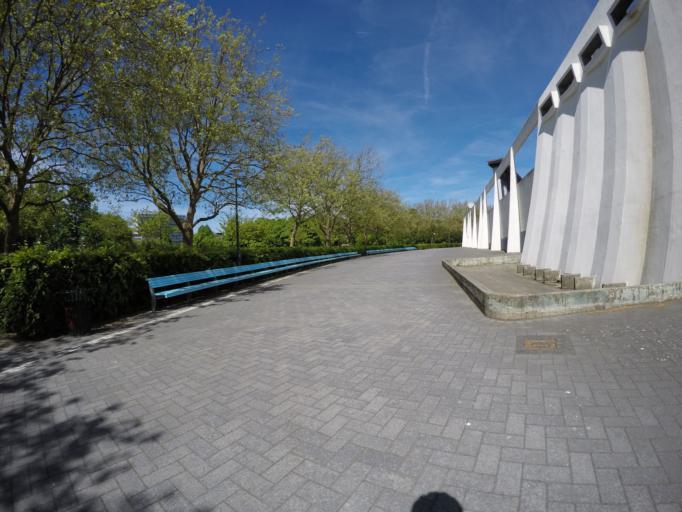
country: SE
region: Skane
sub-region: Malmo
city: Malmoe
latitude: 55.5860
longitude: 12.9873
